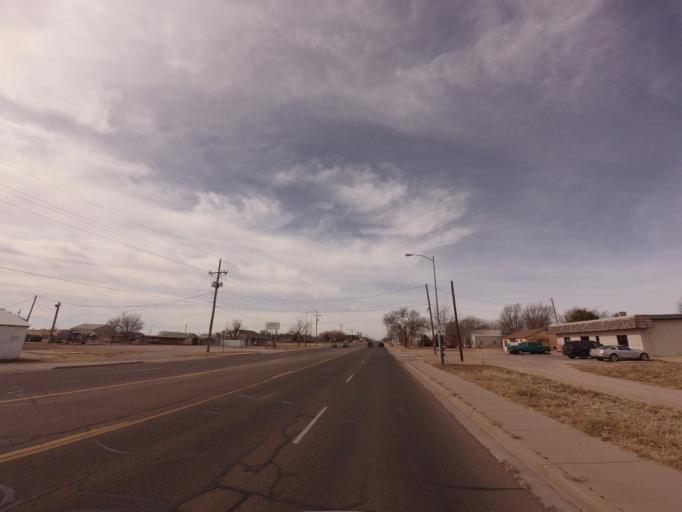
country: US
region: New Mexico
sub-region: Curry County
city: Clovis
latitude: 34.4047
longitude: -103.2332
